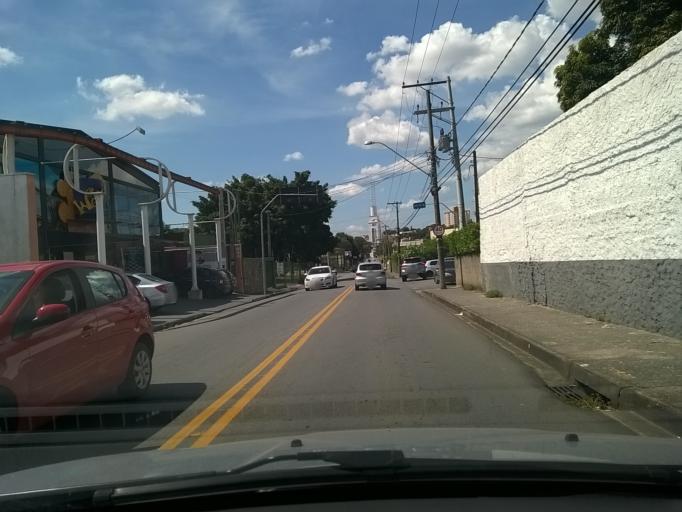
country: BR
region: Sao Paulo
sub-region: Jundiai
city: Jundiai
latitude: -23.2056
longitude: -46.8833
